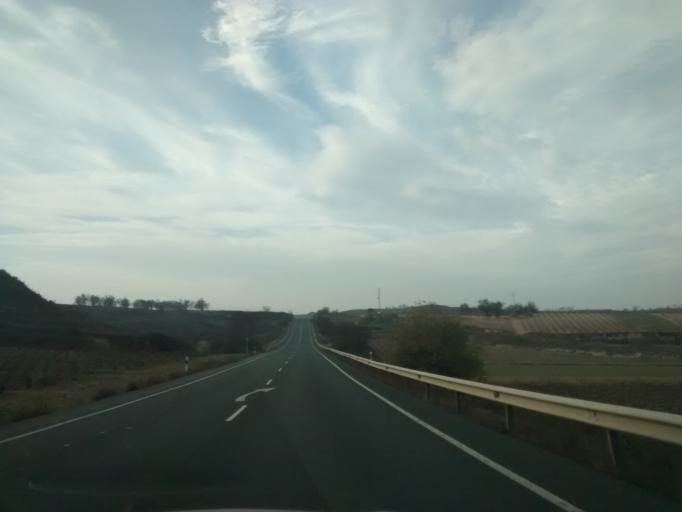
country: ES
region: La Rioja
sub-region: Provincia de La Rioja
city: Briones
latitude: 42.5452
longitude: -2.7947
